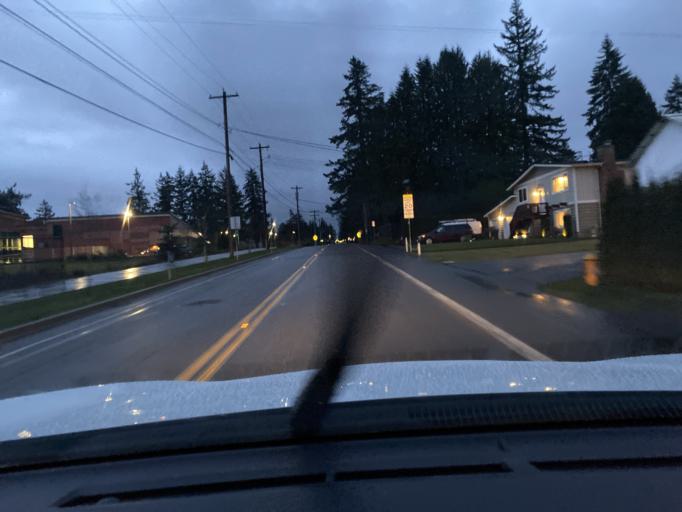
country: US
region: Washington
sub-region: Snohomish County
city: Martha Lake
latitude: 47.8701
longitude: -122.2577
